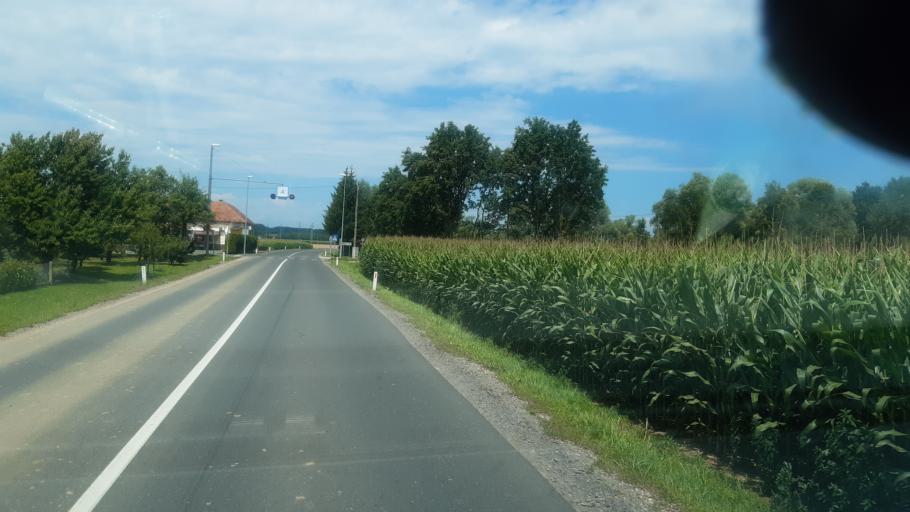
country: SI
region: Murska Sobota
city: Murska Sobota
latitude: 46.6801
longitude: 16.1803
